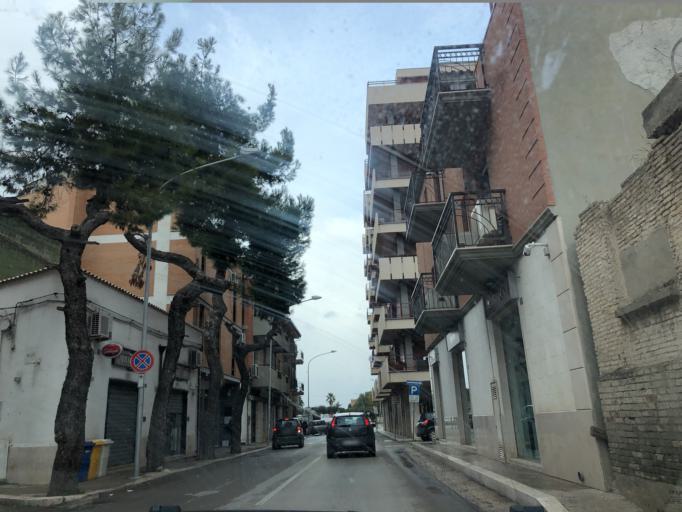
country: IT
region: Apulia
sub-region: Provincia di Foggia
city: Lucera
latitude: 41.5089
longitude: 15.3311
